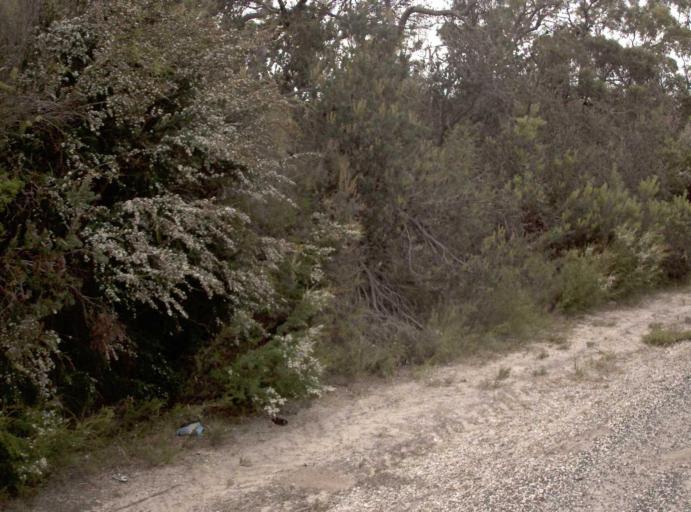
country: AU
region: Victoria
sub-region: East Gippsland
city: Bairnsdale
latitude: -38.1269
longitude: 147.4306
